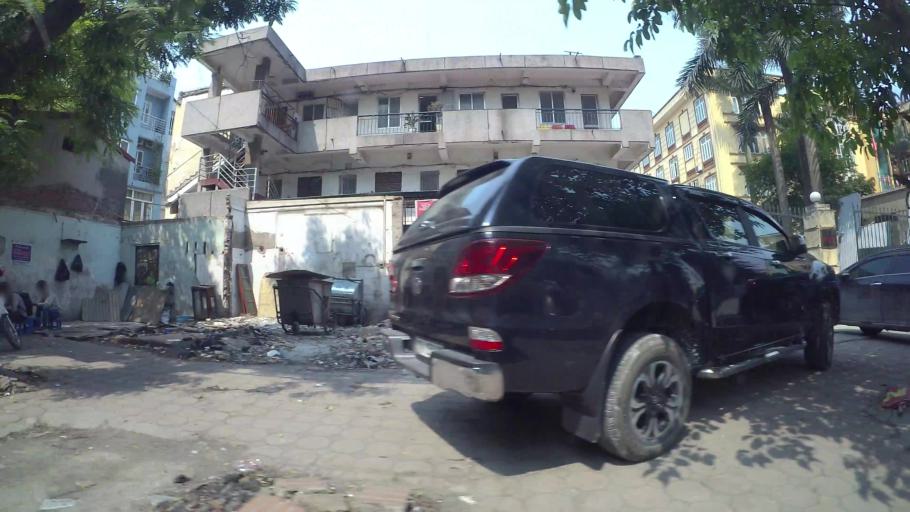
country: VN
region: Ha Noi
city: Thanh Xuan
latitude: 20.9998
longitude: 105.8082
